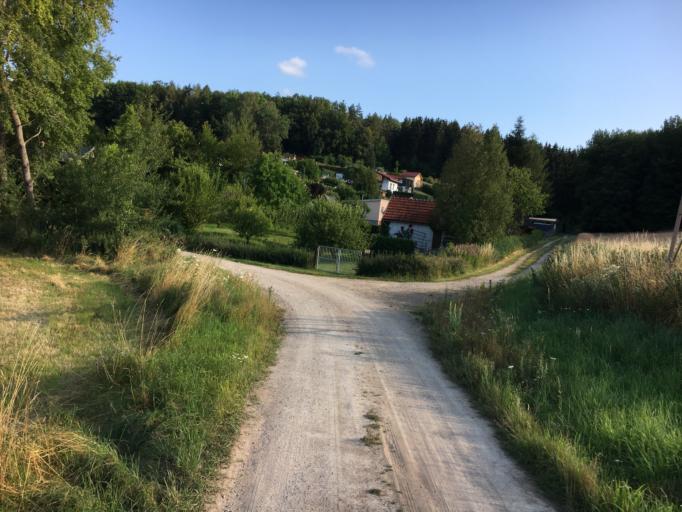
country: DE
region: Thuringia
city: Stadtlengsfeld
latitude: 50.8120
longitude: 10.1244
